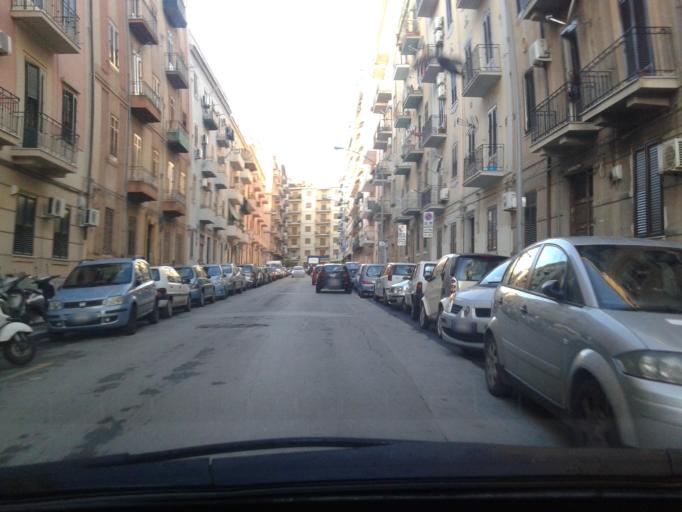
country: IT
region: Sicily
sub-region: Palermo
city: Palermo
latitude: 38.1150
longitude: 13.3452
